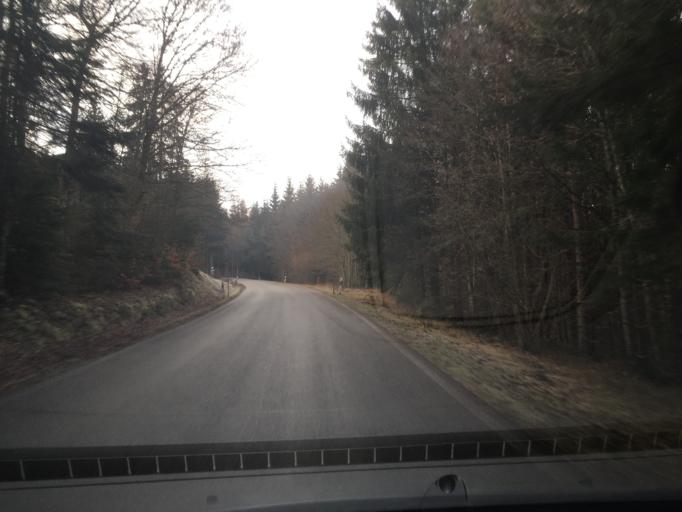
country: DE
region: Baden-Wuerttemberg
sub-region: Freiburg Region
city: Hausern
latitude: 47.7472
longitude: 8.1847
